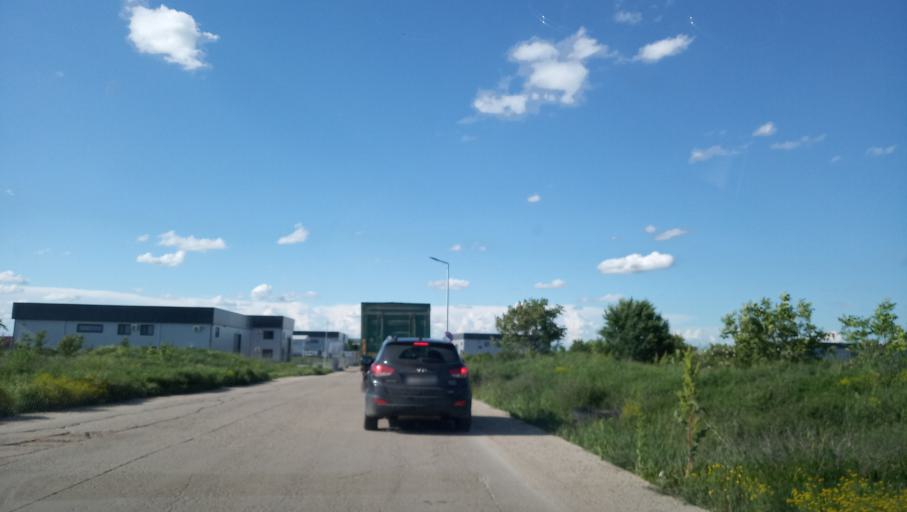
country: RO
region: Ilfov
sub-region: Comuna Dragomiresti-Vale
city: Dragomiresti-Deal
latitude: 44.4498
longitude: 25.9579
